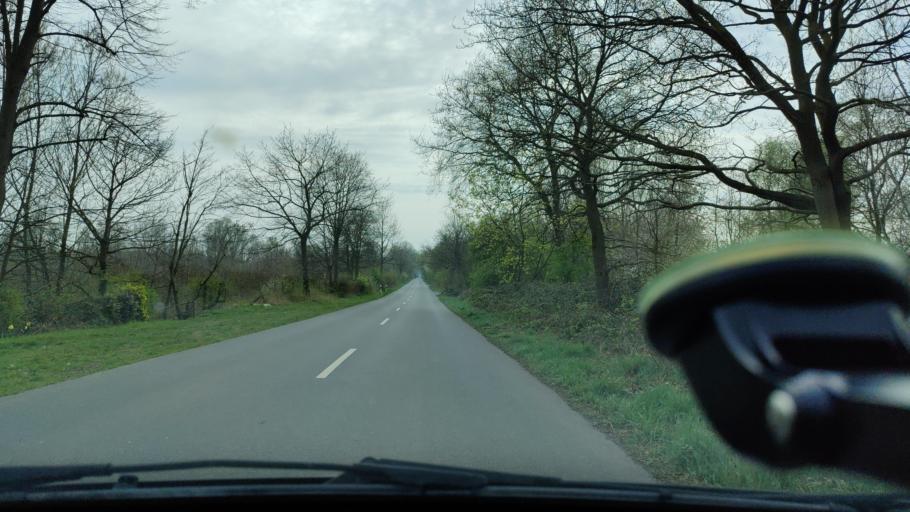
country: DE
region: North Rhine-Westphalia
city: Rheinberg
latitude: 51.5255
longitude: 6.6385
